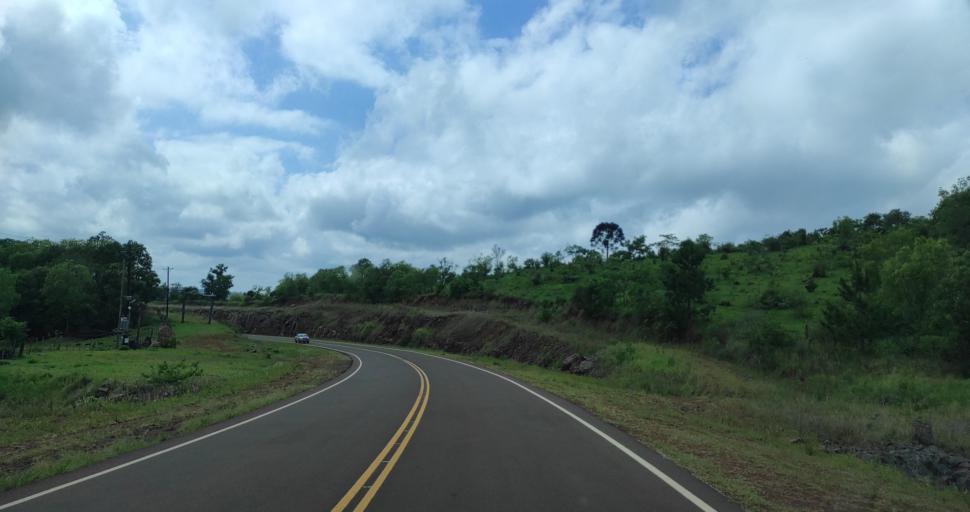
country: AR
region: Misiones
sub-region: Departamento de Veinticinco de Mayo
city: Veinticinco de Mayo
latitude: -27.3770
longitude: -54.8544
